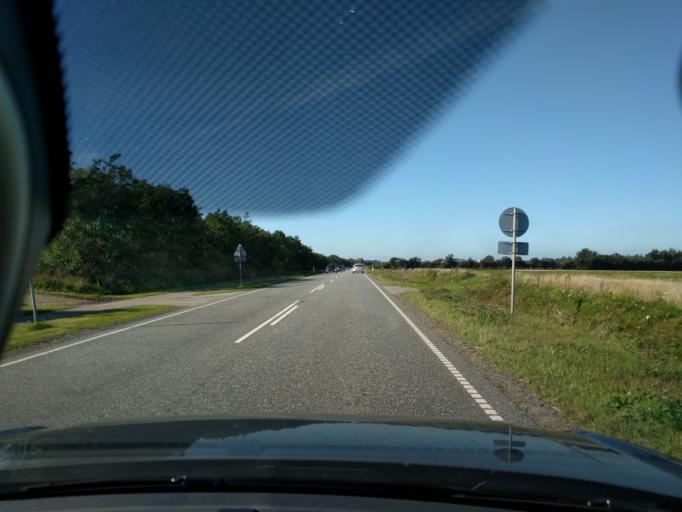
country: DK
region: North Denmark
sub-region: Mariagerfjord Kommune
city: Hobro
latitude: 56.6765
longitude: 9.6720
